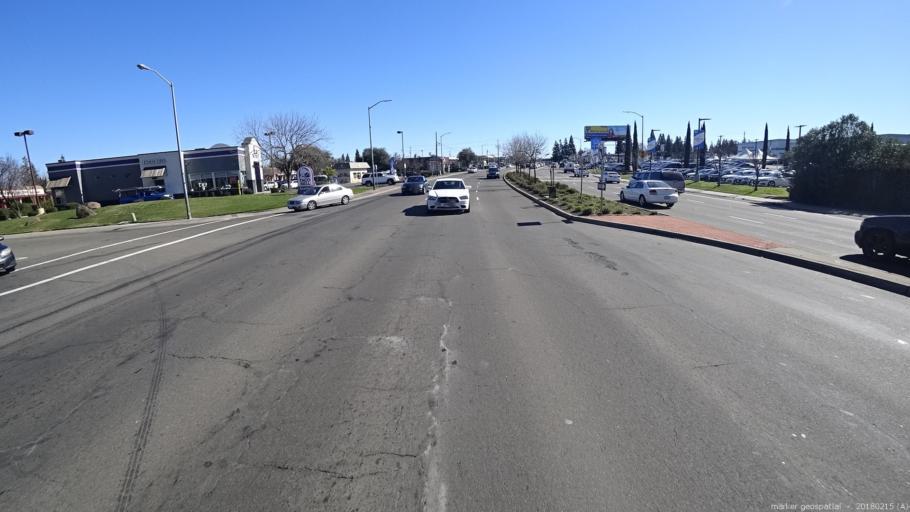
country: US
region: California
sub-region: Sacramento County
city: Foothill Farms
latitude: 38.6804
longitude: -121.3224
